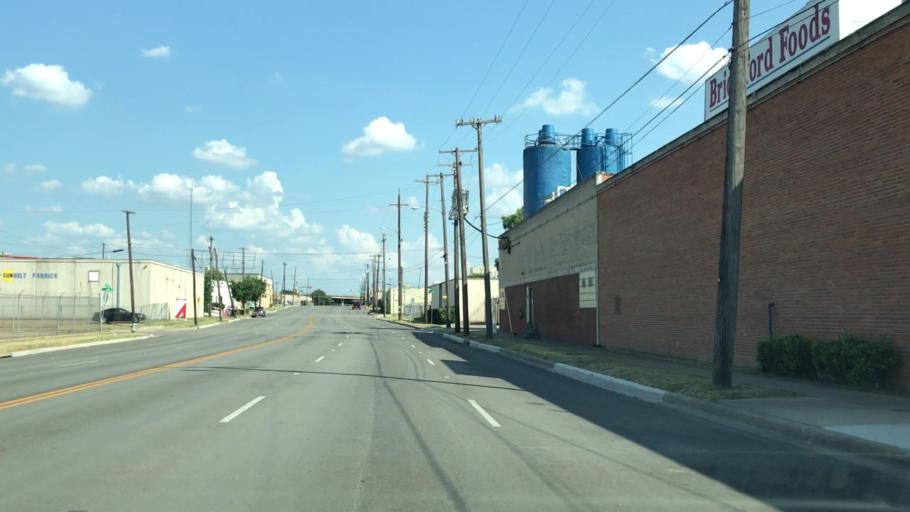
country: US
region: Texas
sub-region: Dallas County
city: Dallas
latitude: 32.7767
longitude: -96.7827
